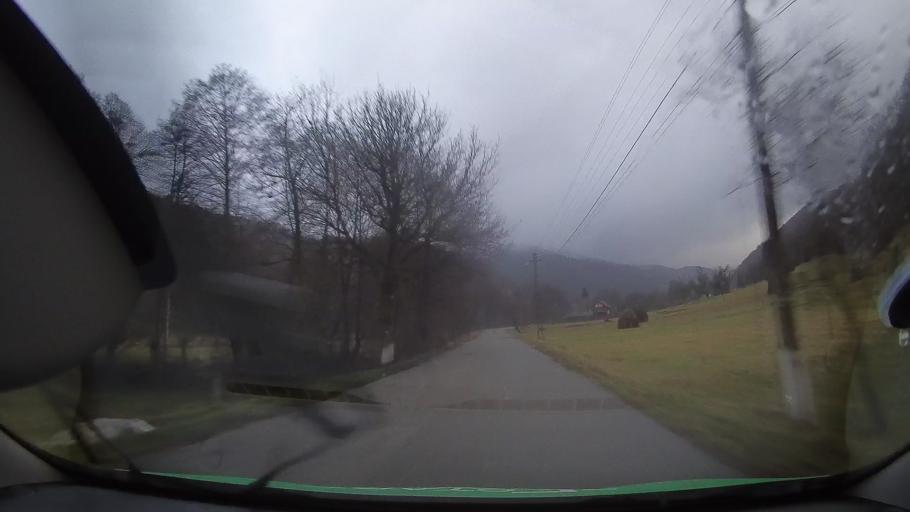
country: RO
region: Hunedoara
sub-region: Comuna Ribita
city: Ribita
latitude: 46.2547
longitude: 22.7484
